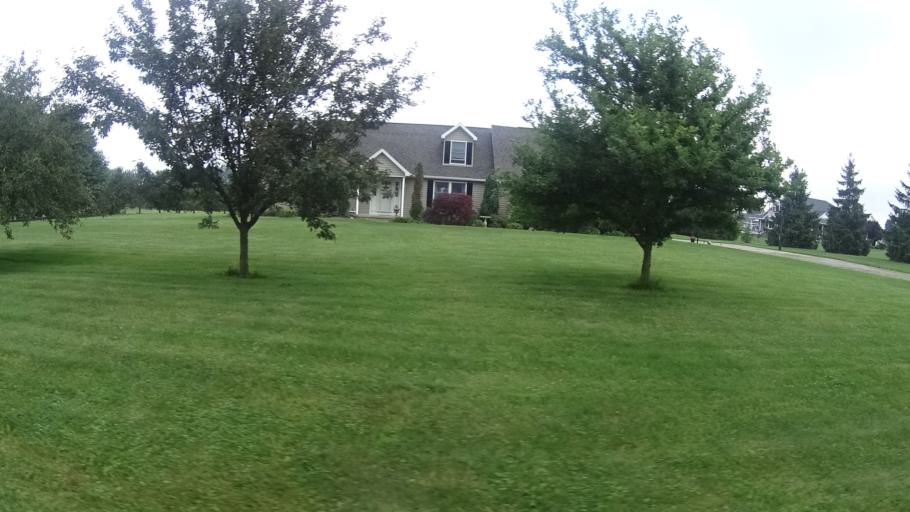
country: US
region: Ohio
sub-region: Erie County
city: Milan
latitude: 41.2975
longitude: -82.5014
